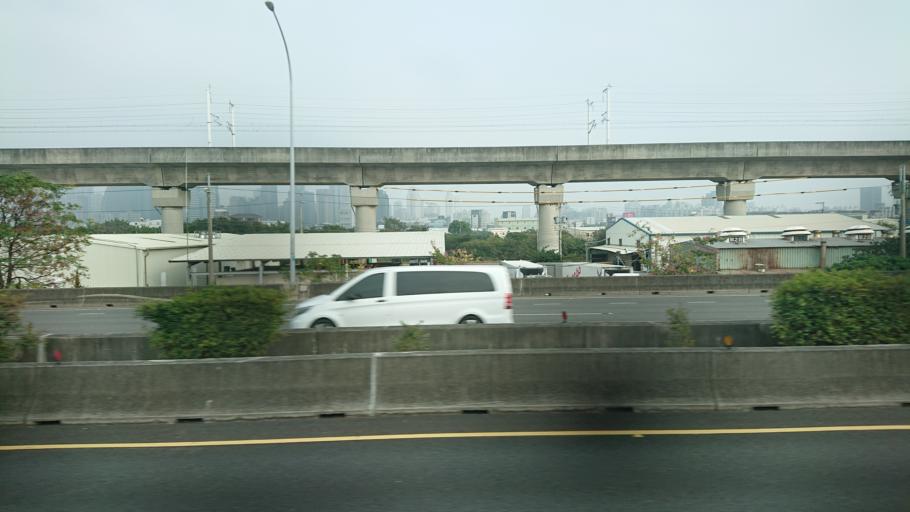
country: TW
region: Taiwan
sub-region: Taichung City
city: Taichung
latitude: 24.1595
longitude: 120.6205
